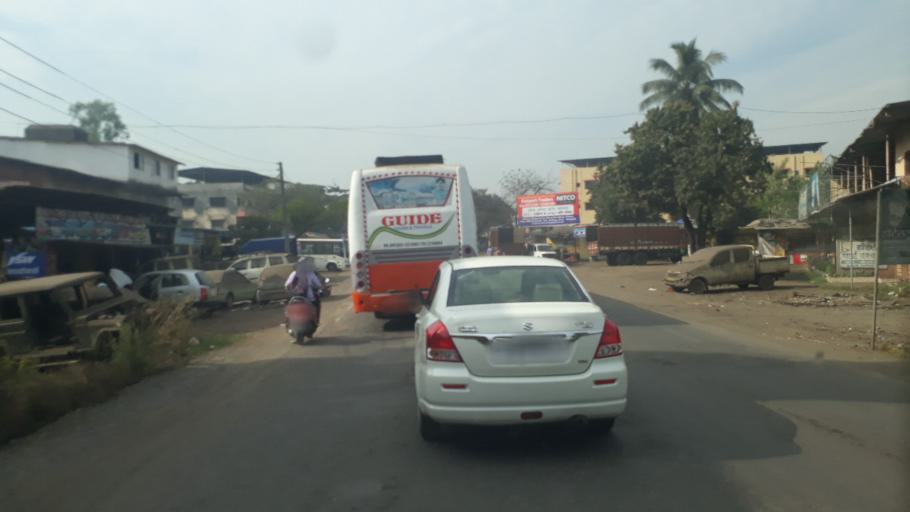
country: IN
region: Maharashtra
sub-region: Raigarh
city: Pen
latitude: 18.7136
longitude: 73.0558
